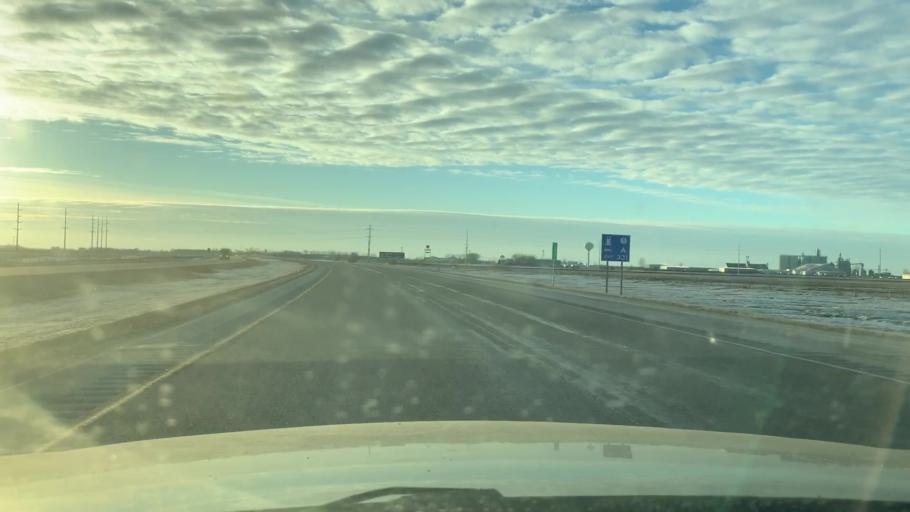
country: US
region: North Dakota
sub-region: Cass County
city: Casselton
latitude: 46.8766
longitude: -97.1944
